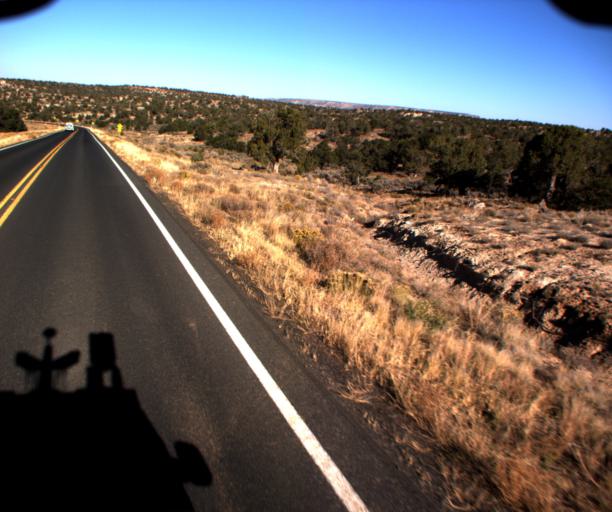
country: US
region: Arizona
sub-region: Apache County
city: Ganado
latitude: 35.7663
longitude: -109.7908
